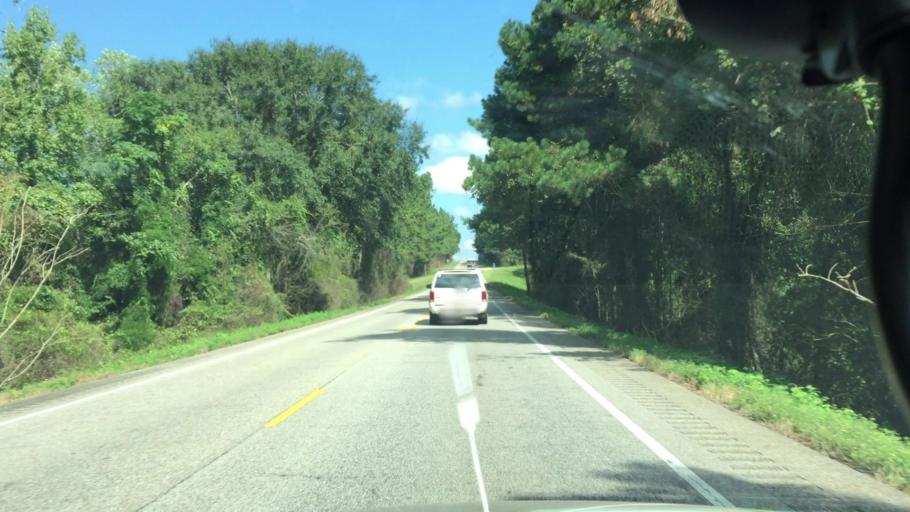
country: US
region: Alabama
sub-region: Coffee County
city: New Brockton
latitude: 31.4046
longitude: -85.8817
